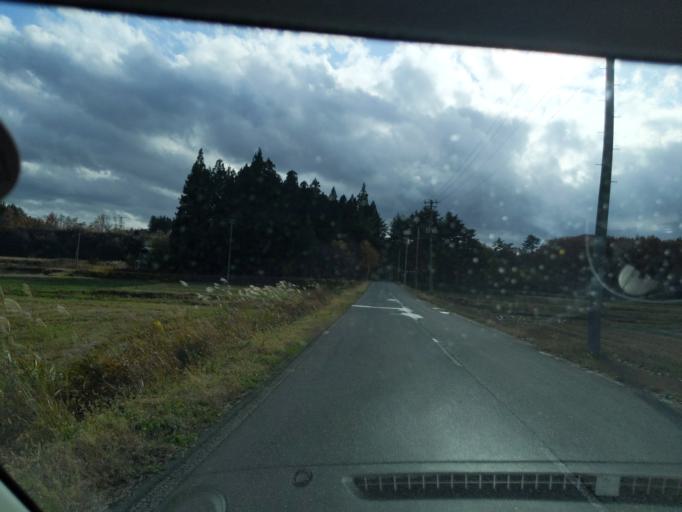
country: JP
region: Iwate
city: Mizusawa
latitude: 39.1076
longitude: 140.9719
